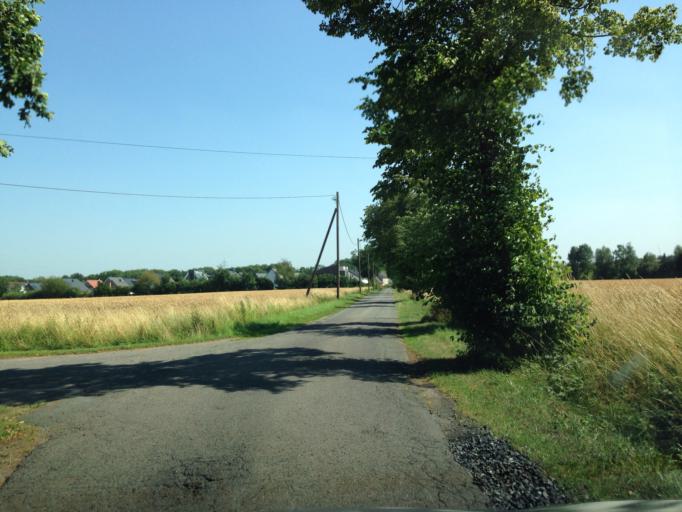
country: DE
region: North Rhine-Westphalia
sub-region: Regierungsbezirk Munster
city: Altenberge
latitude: 51.9962
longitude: 7.5382
